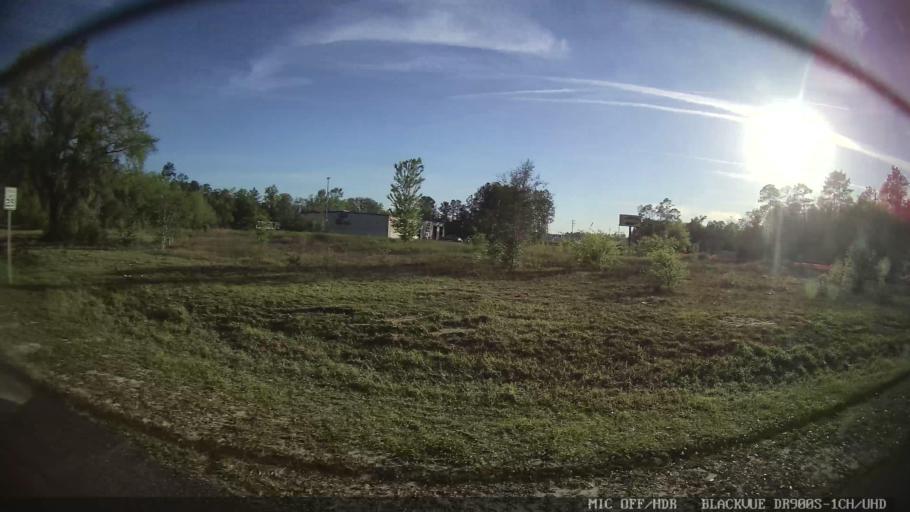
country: US
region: Georgia
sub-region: Echols County
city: Statenville
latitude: 30.6474
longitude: -83.1824
